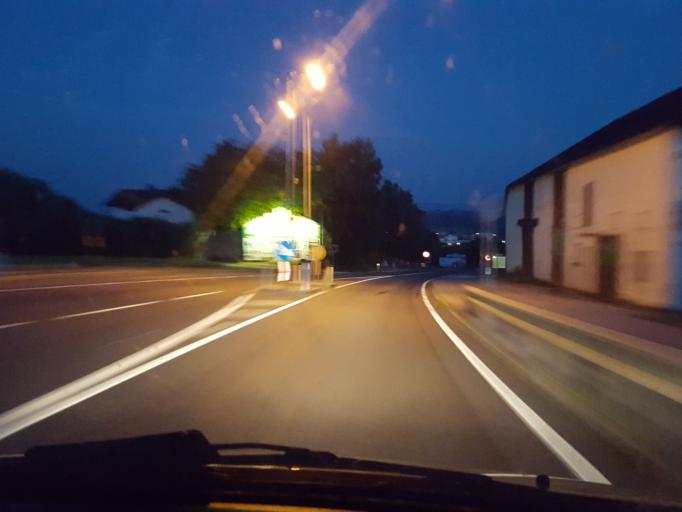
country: AT
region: Lower Austria
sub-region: Politischer Bezirk Scheibbs
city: Wieselburg
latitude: 48.1434
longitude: 15.1343
